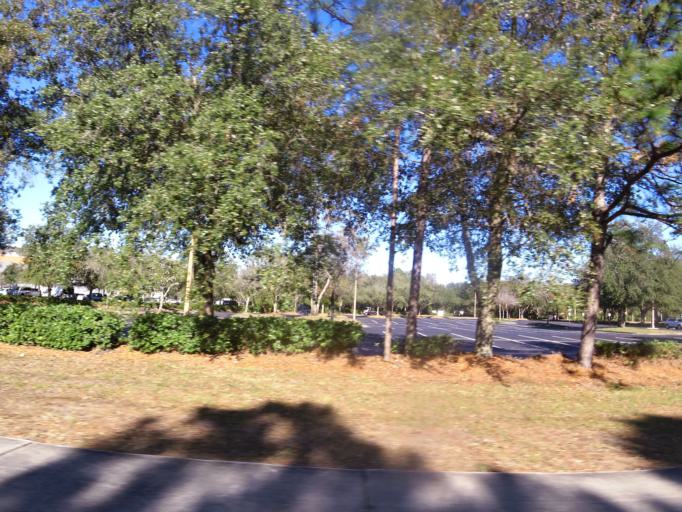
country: US
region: Florida
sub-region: Duval County
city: Jacksonville
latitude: 30.2437
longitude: -81.5876
